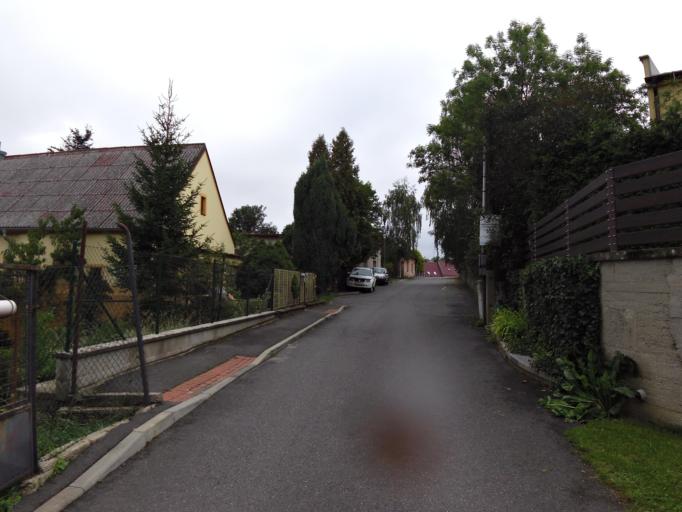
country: CZ
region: Jihocesky
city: Mlada Vozice
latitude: 49.5335
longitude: 14.8074
